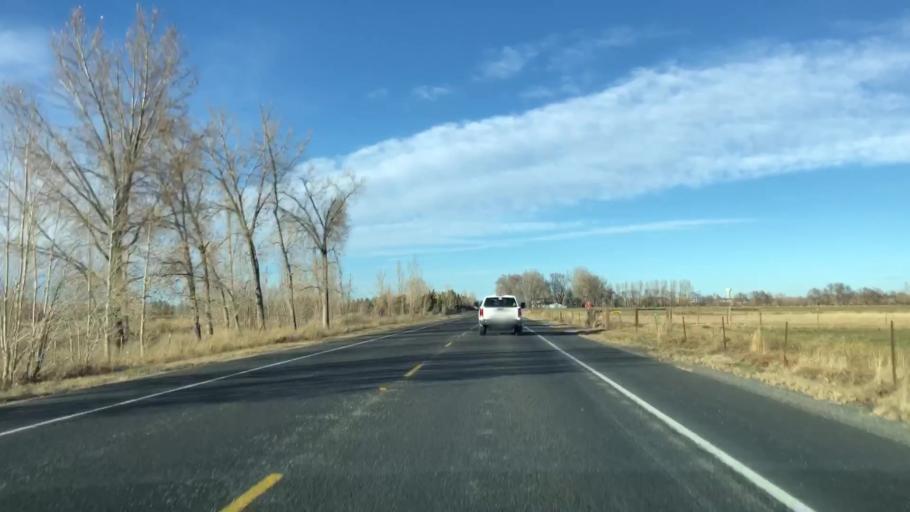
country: US
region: Colorado
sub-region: Weld County
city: Windsor
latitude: 40.5037
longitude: -104.9818
